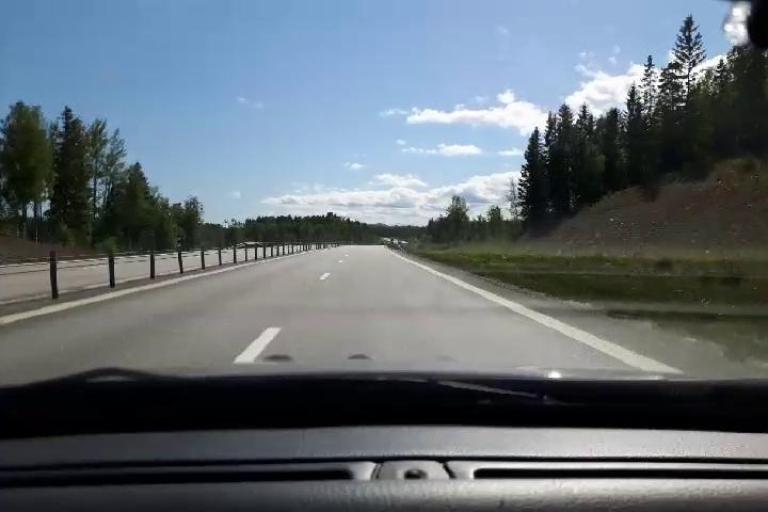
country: SE
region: Gaevleborg
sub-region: Hudiksvalls Kommun
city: Iggesund
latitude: 61.6698
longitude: 17.0293
